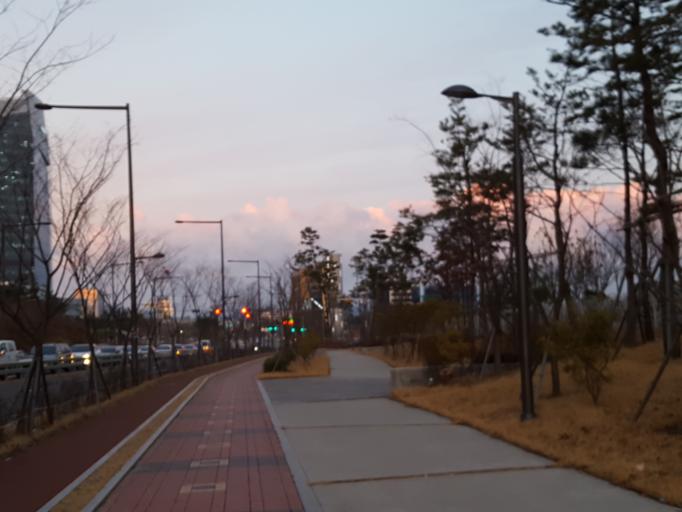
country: KR
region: Ulsan
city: Ulsan
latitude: 35.5635
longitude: 129.3043
